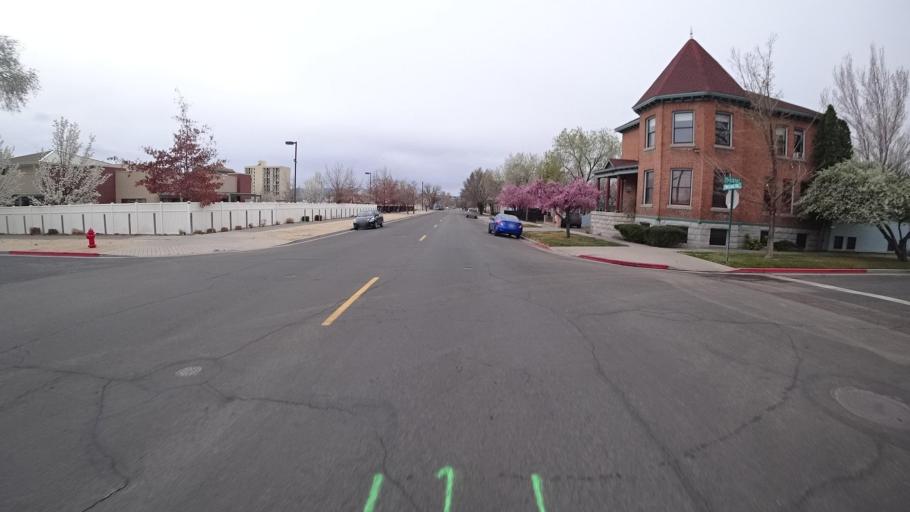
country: US
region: Nevada
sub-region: Washoe County
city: Reno
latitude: 39.5309
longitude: -119.8243
